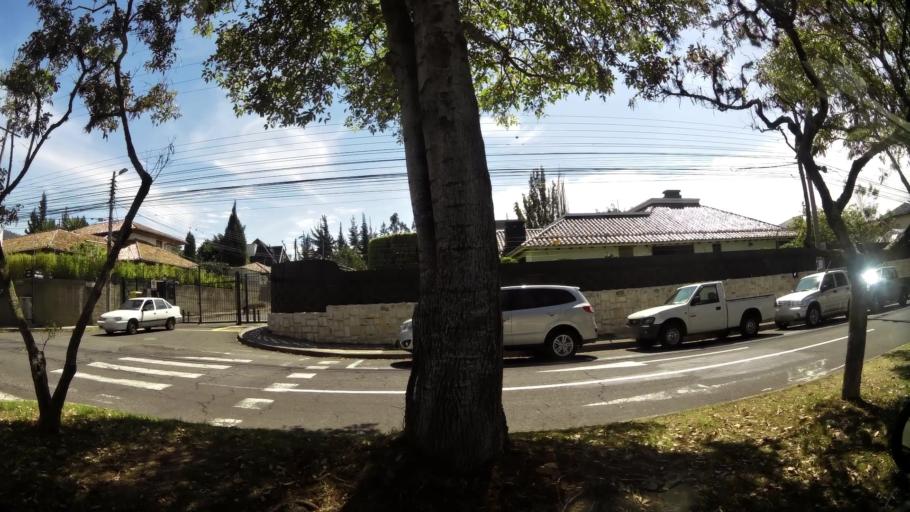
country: EC
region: Pichincha
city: Quito
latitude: -0.1946
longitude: -78.4376
